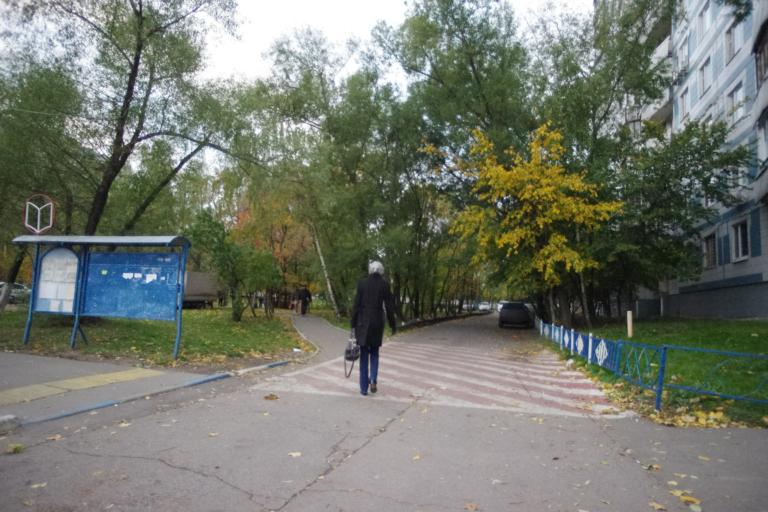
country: RU
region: Moskovskaya
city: Semenovskoye
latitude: 55.6619
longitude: 37.5329
